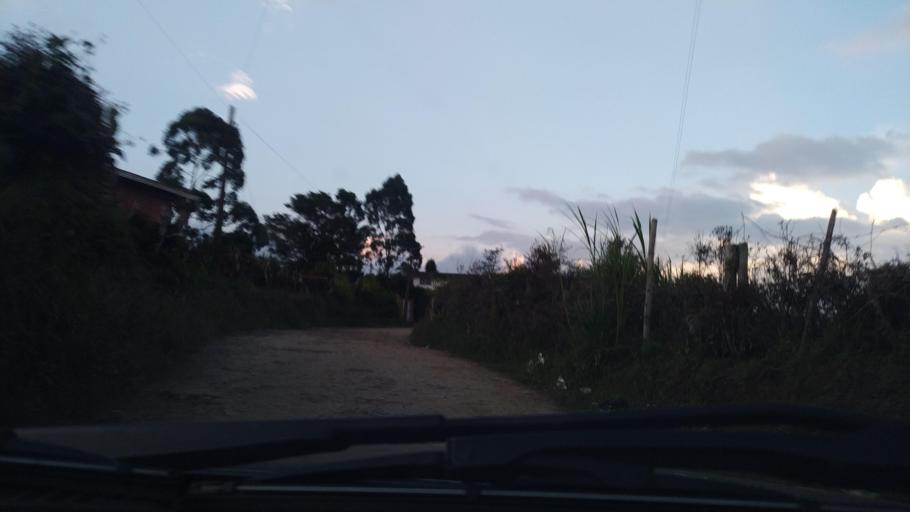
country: CO
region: Antioquia
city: Marinilla
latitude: 6.1922
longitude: -75.2831
